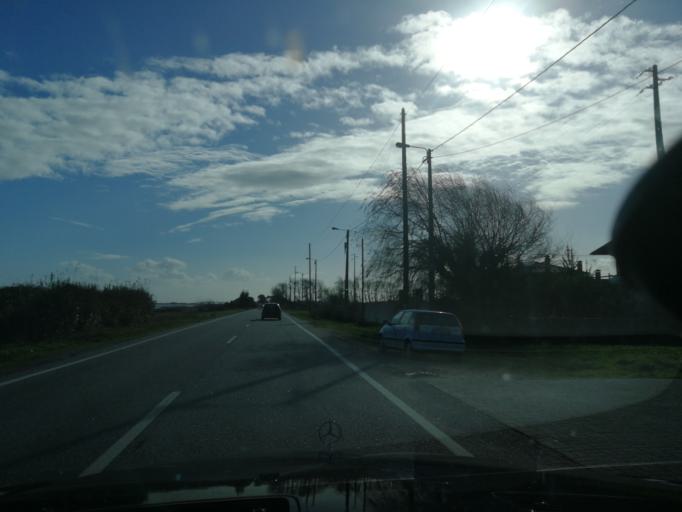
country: PT
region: Aveiro
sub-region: Estarreja
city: Pardilho
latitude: 40.8147
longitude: -8.6706
